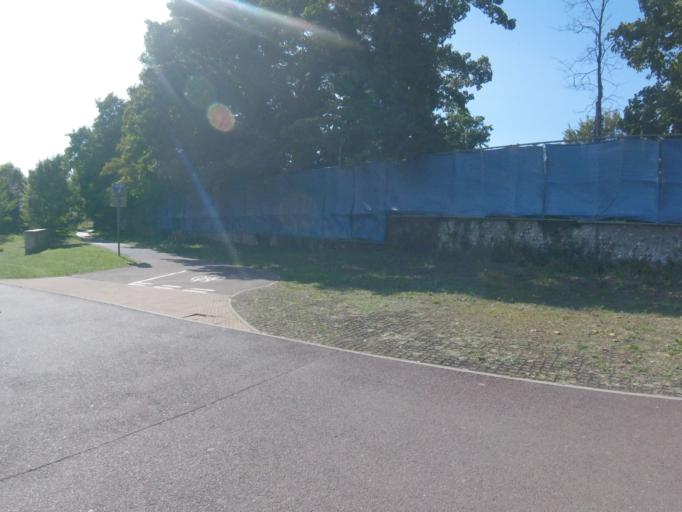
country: GB
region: England
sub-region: Brighton and Hove
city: Rottingdean
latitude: 50.8632
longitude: -0.0886
